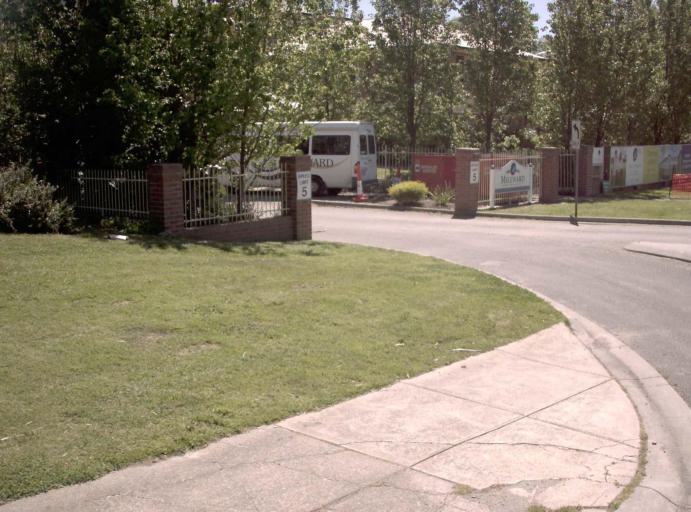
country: AU
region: Victoria
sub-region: Whitehorse
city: Blackburn North
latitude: -37.7994
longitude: 145.1599
